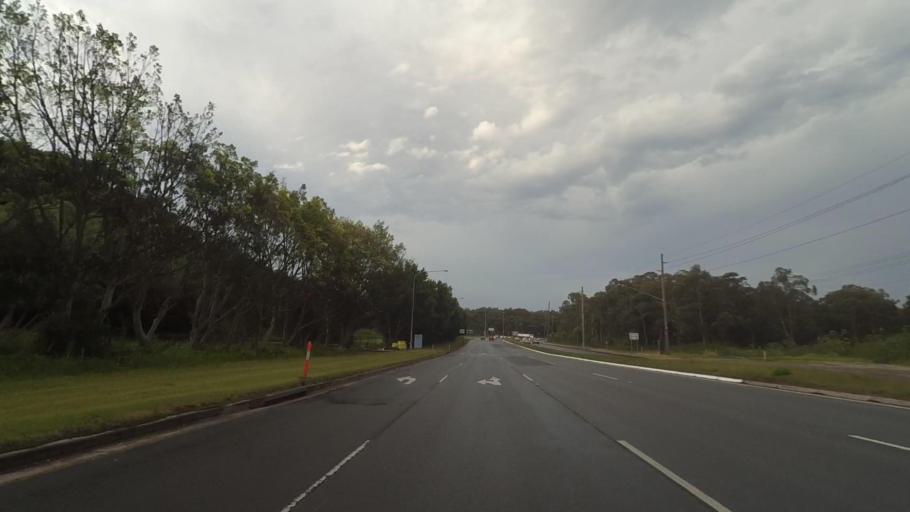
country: AU
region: New South Wales
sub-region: Wollongong
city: Mount Saint Thomas
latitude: -34.4485
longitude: 150.8750
